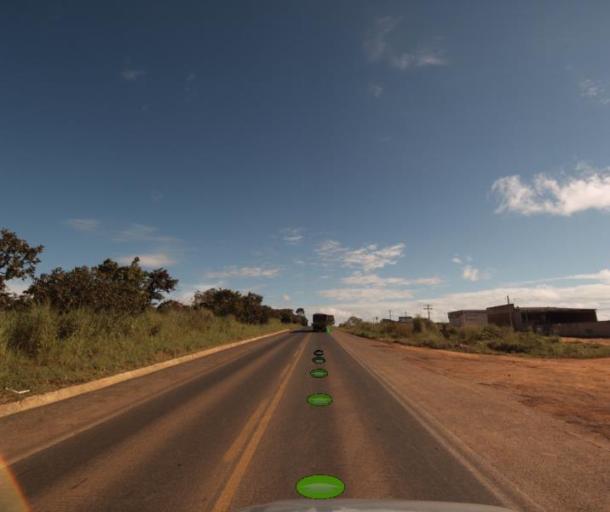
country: BR
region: Goias
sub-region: Uruacu
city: Uruacu
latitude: -14.5479
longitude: -49.1604
